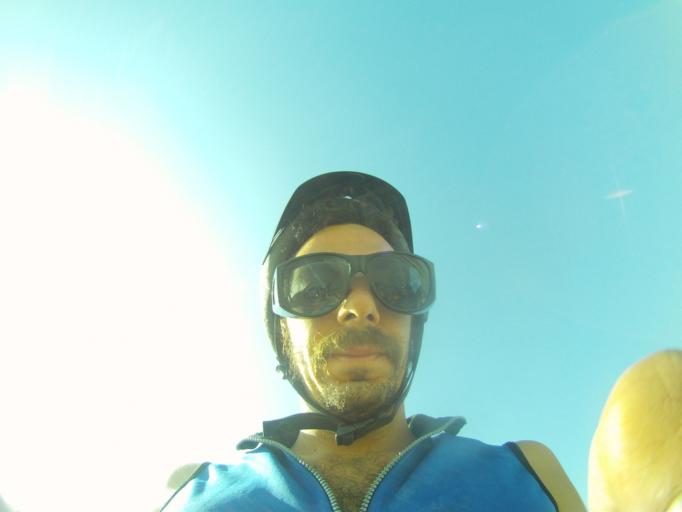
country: KZ
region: Ongtustik Qazaqstan
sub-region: Tulkibas Audany
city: Zhabagly
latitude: 42.6649
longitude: 70.8020
